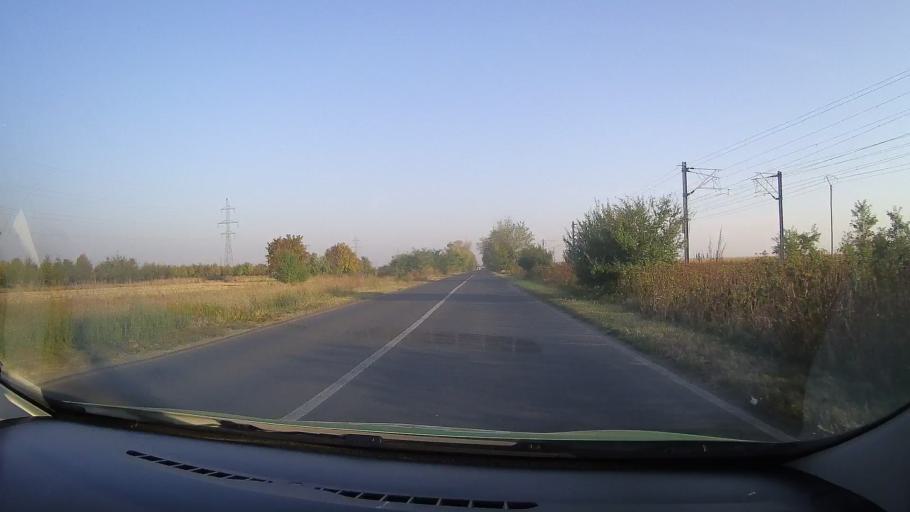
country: RO
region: Arad
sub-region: Comuna Curtici
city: Curtici
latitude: 46.3187
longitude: 21.3070
